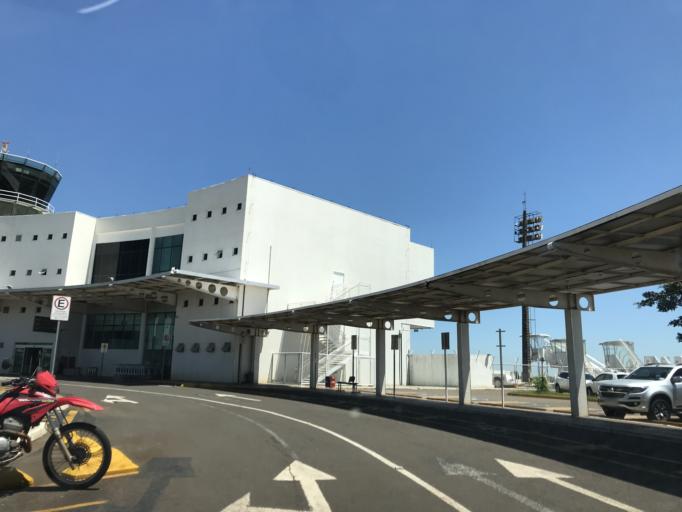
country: BR
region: Parana
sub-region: Paicandu
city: Paicandu
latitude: -23.4799
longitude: -52.0117
